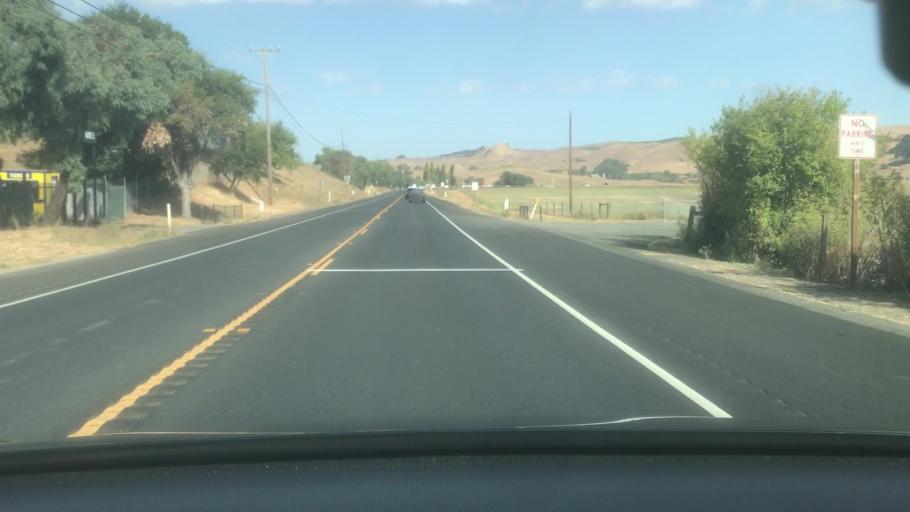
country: US
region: California
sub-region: Marin County
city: Black Point-Green Point
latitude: 38.1633
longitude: -122.4537
